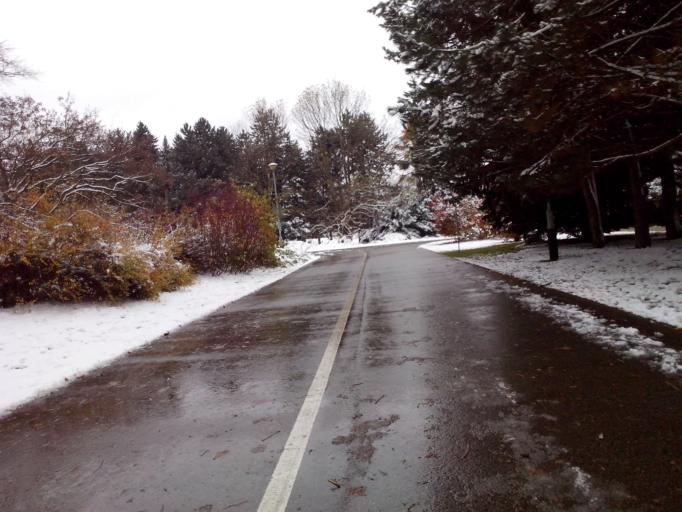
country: PL
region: Subcarpathian Voivodeship
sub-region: Rzeszow
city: Rzeszow
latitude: 50.0239
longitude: 21.9997
